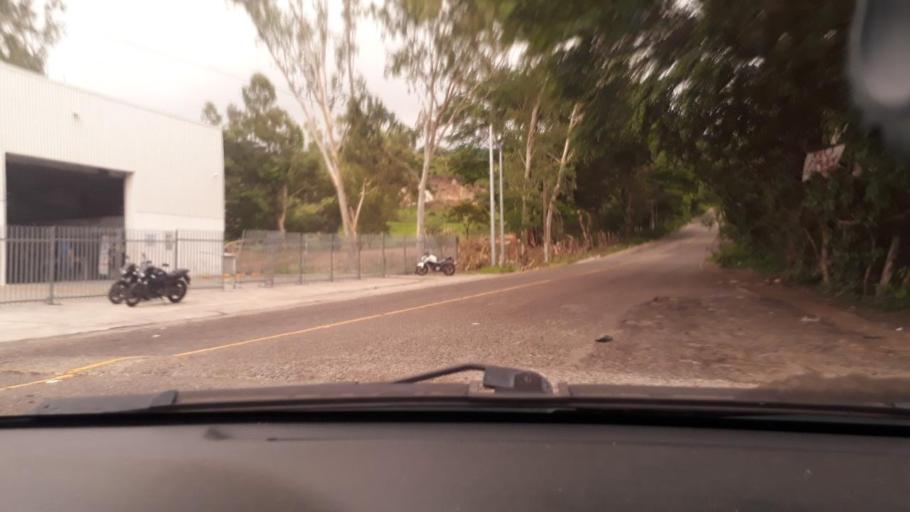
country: GT
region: Jutiapa
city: Jalpatagua
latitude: 14.1589
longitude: -90.0539
